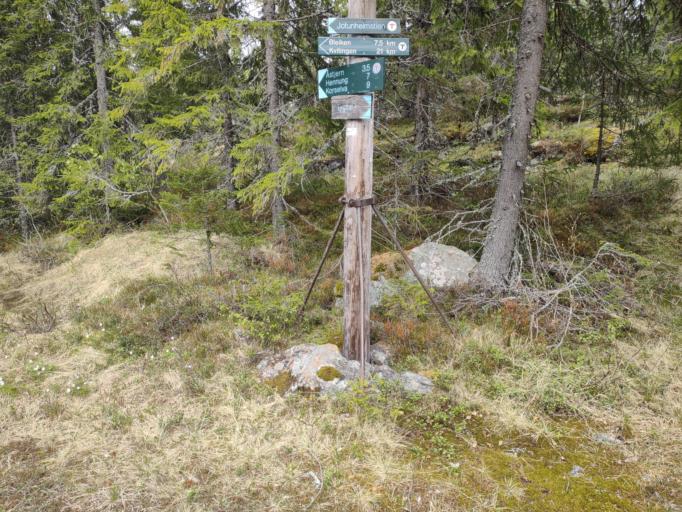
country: NO
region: Oppland
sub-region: Gran
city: Jaren
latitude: 60.4674
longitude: 10.5785
